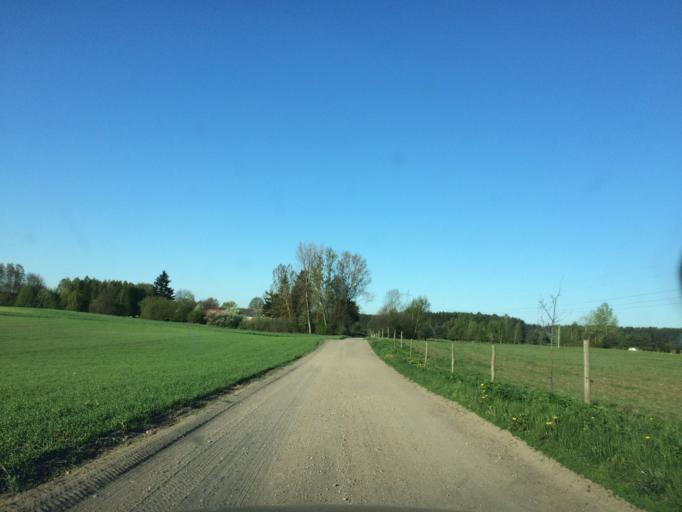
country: PL
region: Warmian-Masurian Voivodeship
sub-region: Powiat dzialdowski
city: Rybno
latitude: 53.4230
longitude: 19.9156
